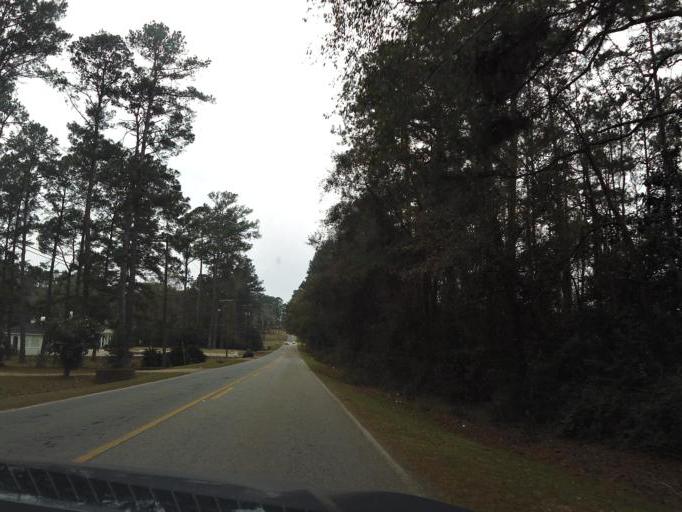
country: US
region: Georgia
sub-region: Thomas County
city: Thomasville
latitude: 30.8142
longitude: -83.9516
